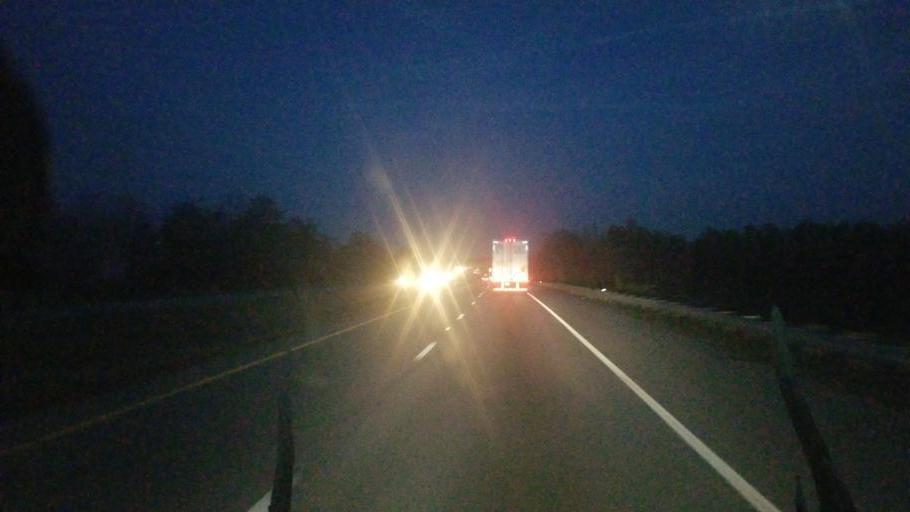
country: US
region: Ohio
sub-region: Belmont County
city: Barnesville
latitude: 40.0559
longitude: -81.2841
